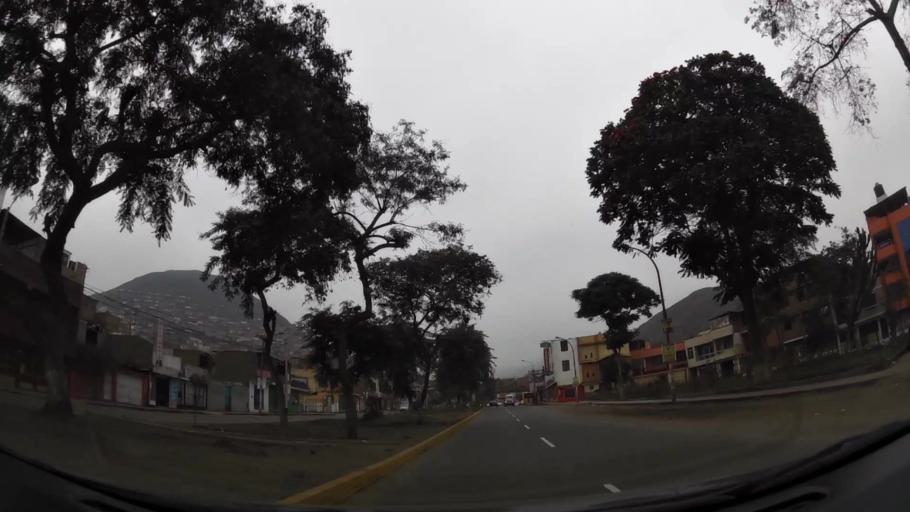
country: PE
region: Lima
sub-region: Lima
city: Urb. Santo Domingo
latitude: -11.9076
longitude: -77.0349
